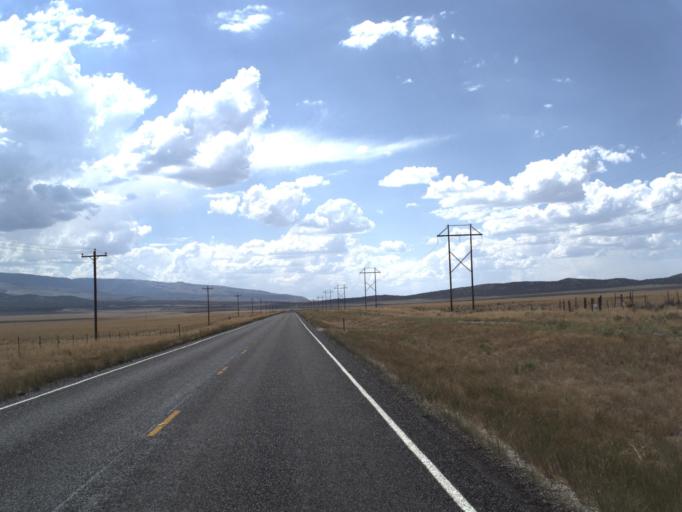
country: US
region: Idaho
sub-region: Power County
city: American Falls
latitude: 41.9665
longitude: -113.0738
